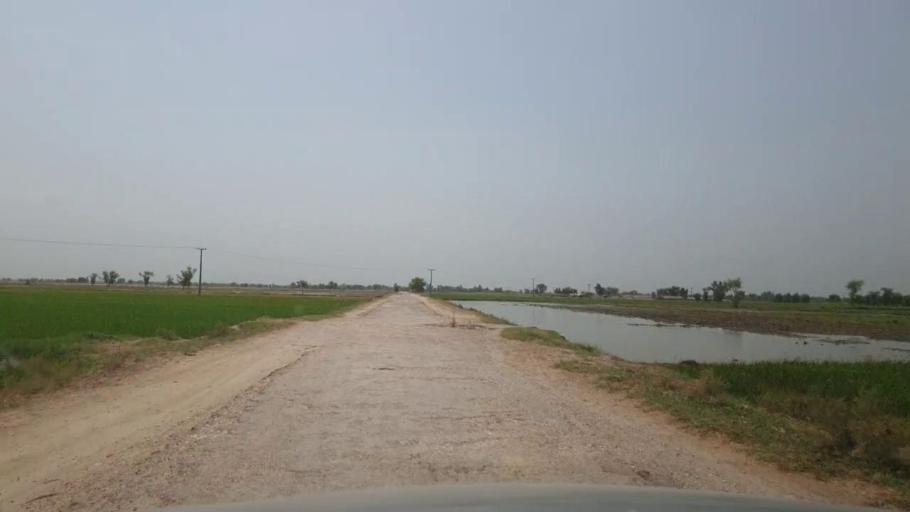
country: PK
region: Sindh
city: Garhi Yasin
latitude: 27.9179
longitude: 68.4039
